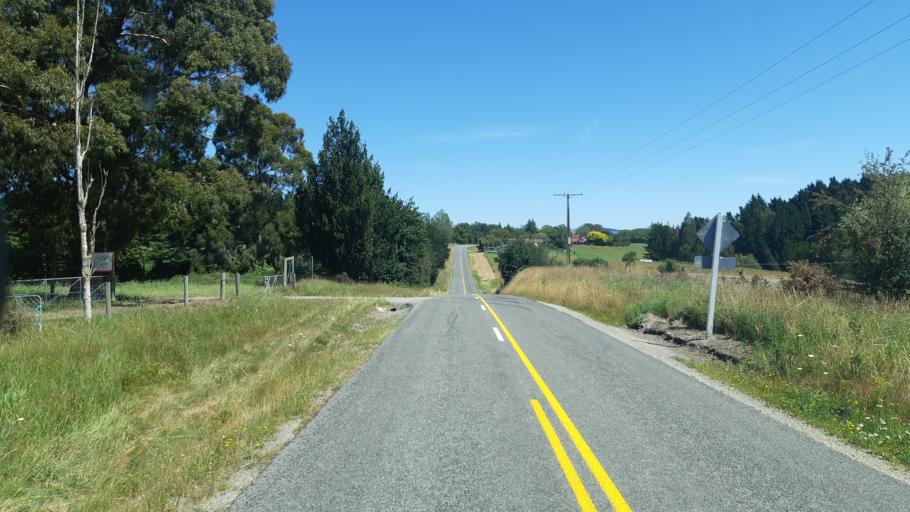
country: NZ
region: Canterbury
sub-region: Timaru District
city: Timaru
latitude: -44.4081
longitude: 171.1491
